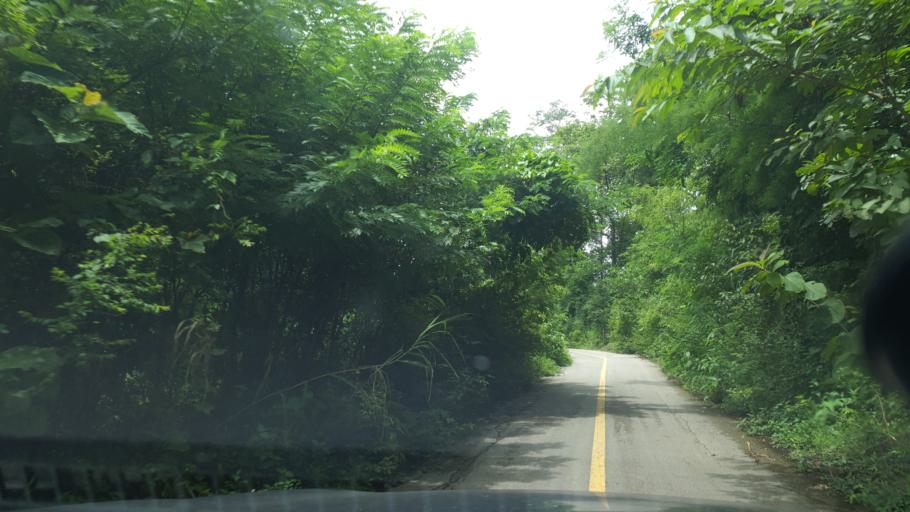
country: TH
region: Lampang
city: Hang Chat
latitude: 18.3517
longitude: 99.2531
